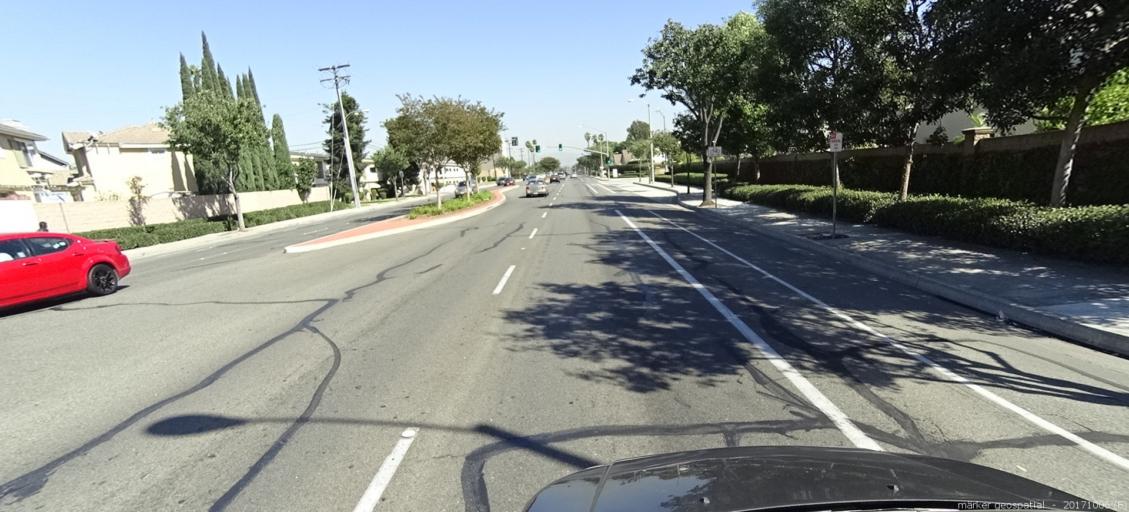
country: US
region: California
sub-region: Orange County
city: Garden Grove
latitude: 33.7887
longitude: -117.9397
